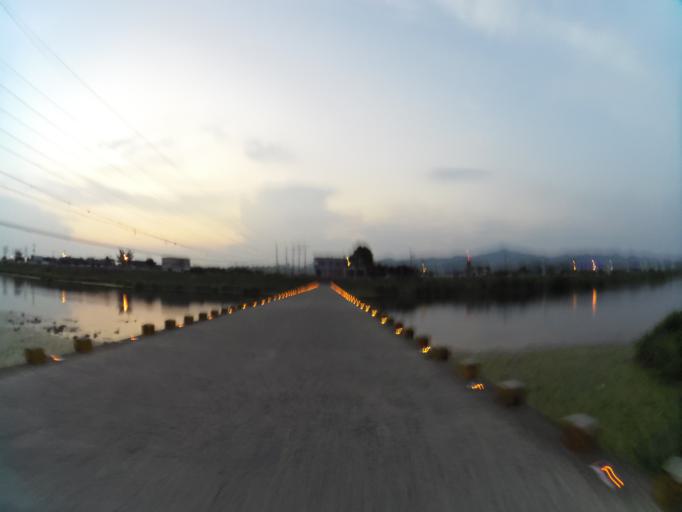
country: KR
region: Gyeongsangbuk-do
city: Gyeongsan-si
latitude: 35.8574
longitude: 128.7395
